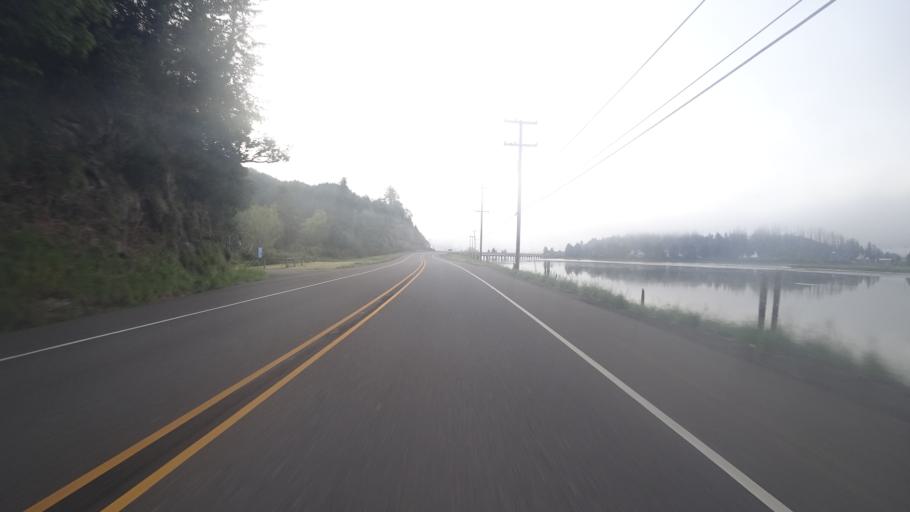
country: US
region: Oregon
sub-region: Douglas County
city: Reedsport
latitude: 43.7208
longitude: -124.1060
